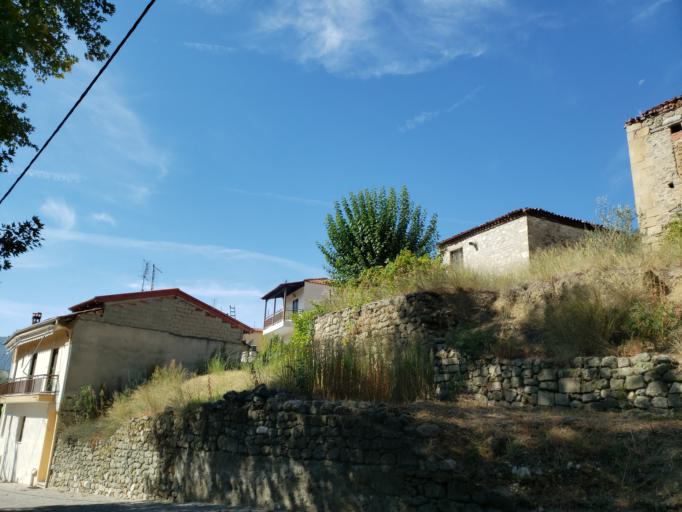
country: GR
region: Thessaly
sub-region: Trikala
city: Kalampaka
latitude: 39.7099
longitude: 21.6306
